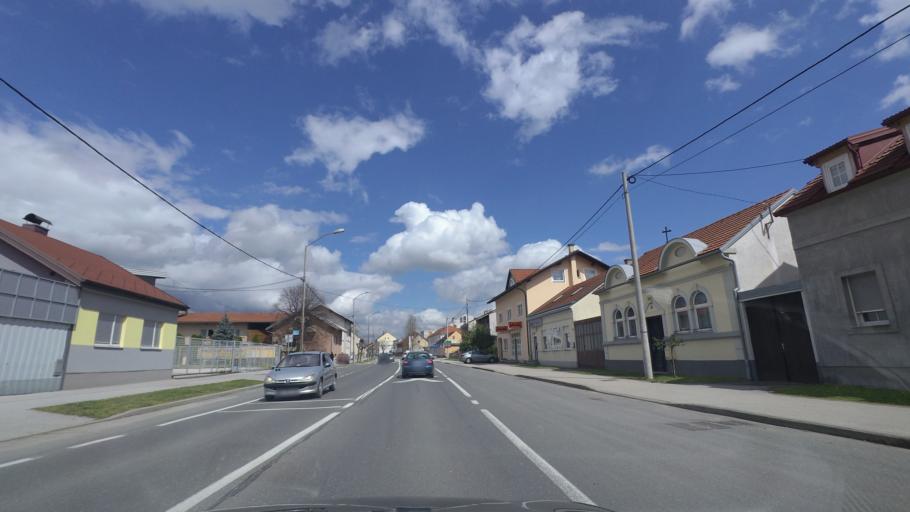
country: HR
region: Zagrebacka
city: Jastrebarsko
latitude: 45.6660
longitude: 15.6460
